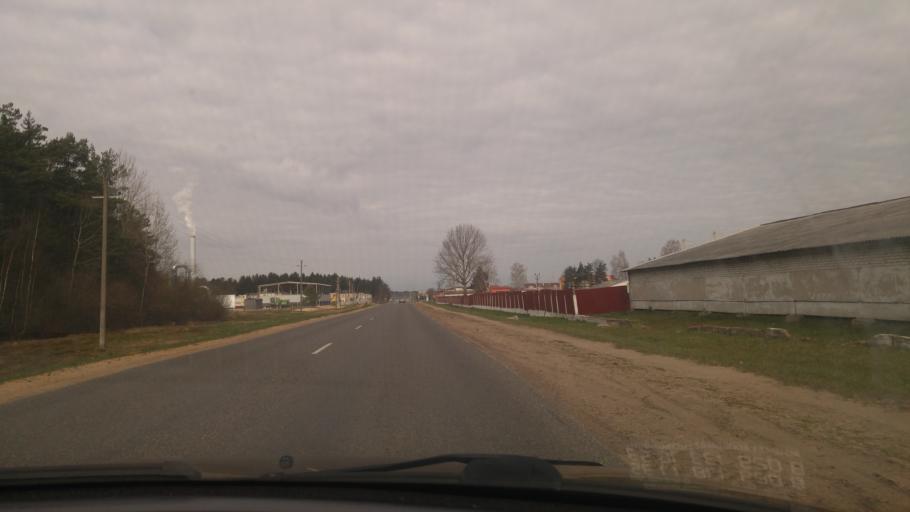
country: BY
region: Minsk
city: Chervyen'
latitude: 53.6967
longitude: 28.4280
